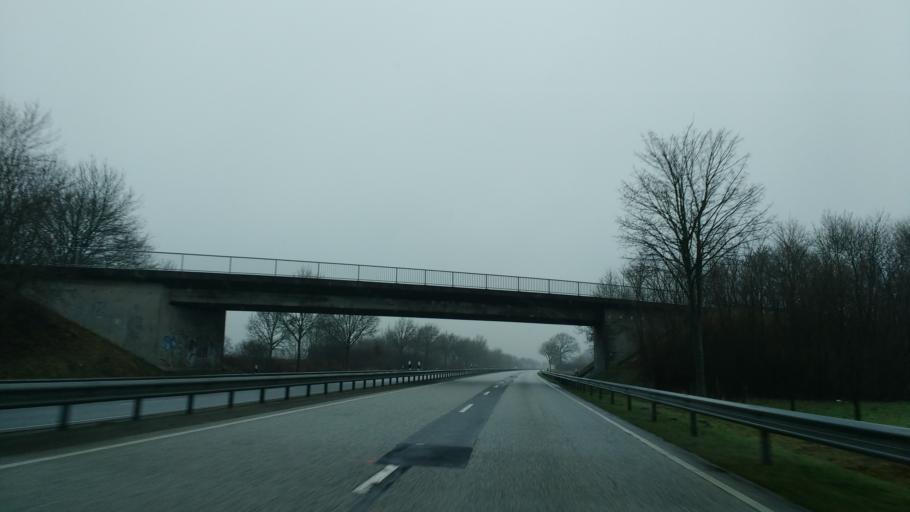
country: DE
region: Schleswig-Holstein
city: Jevenstedt
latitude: 54.2576
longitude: 9.6663
